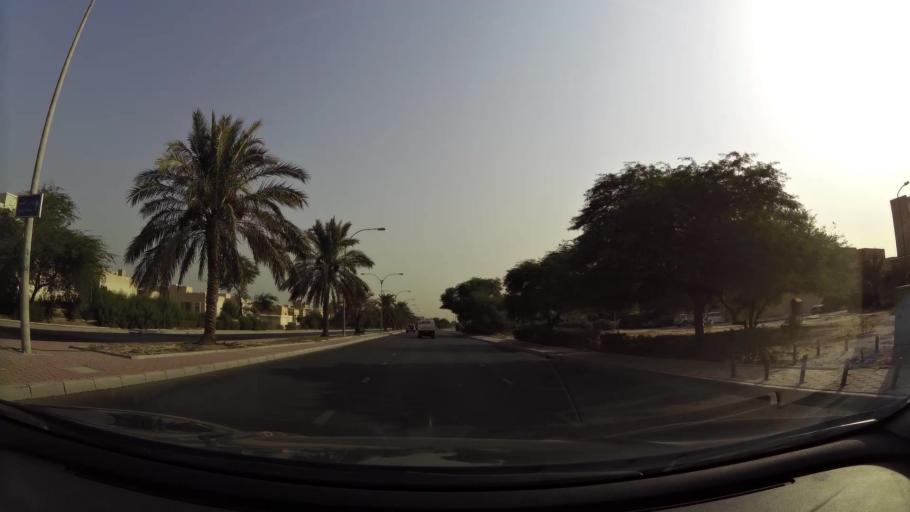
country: KW
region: Al Ahmadi
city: Ar Riqqah
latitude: 29.1323
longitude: 48.1031
